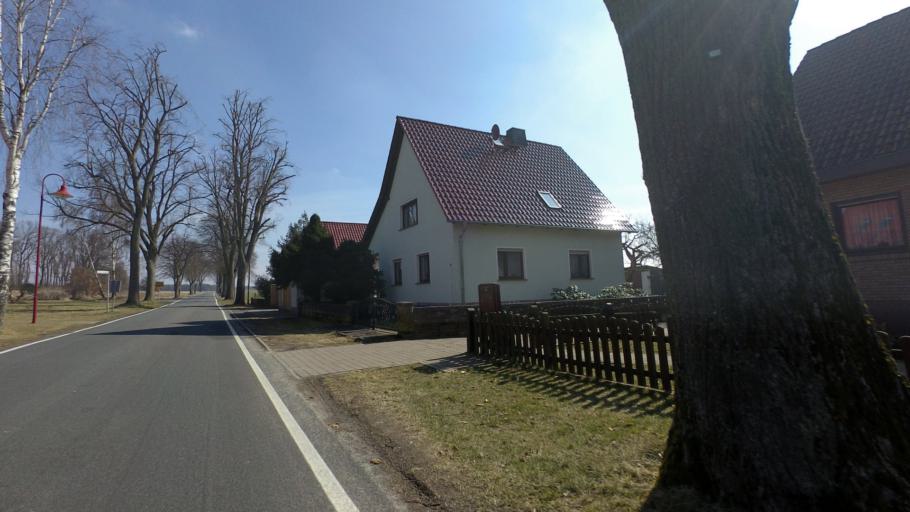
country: DE
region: Saxony-Anhalt
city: Nudersdorf
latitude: 52.0215
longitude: 12.5362
